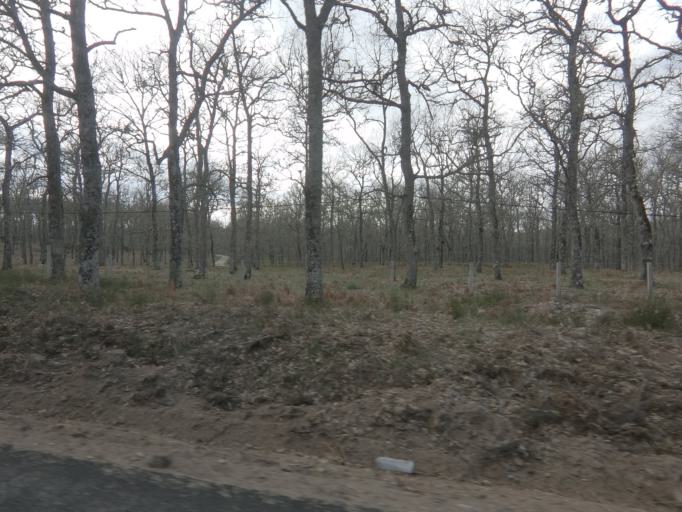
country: ES
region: Castille and Leon
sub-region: Provincia de Salamanca
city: Villasrubias
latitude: 40.3280
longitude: -6.6451
